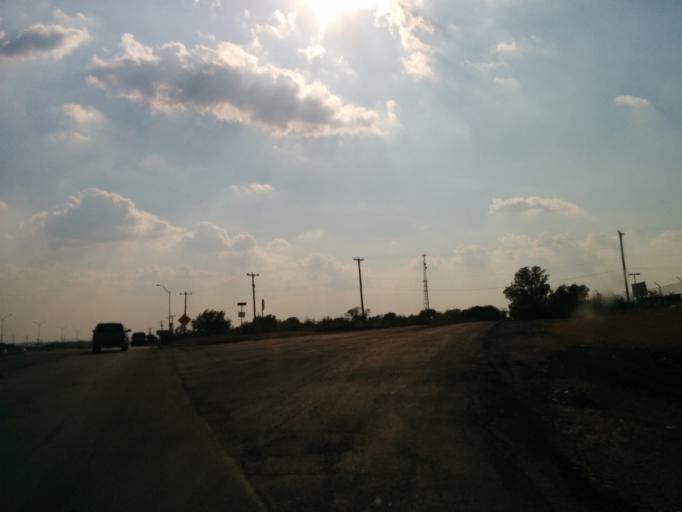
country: US
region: Texas
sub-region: Bexar County
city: Converse
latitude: 29.4657
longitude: -98.2932
